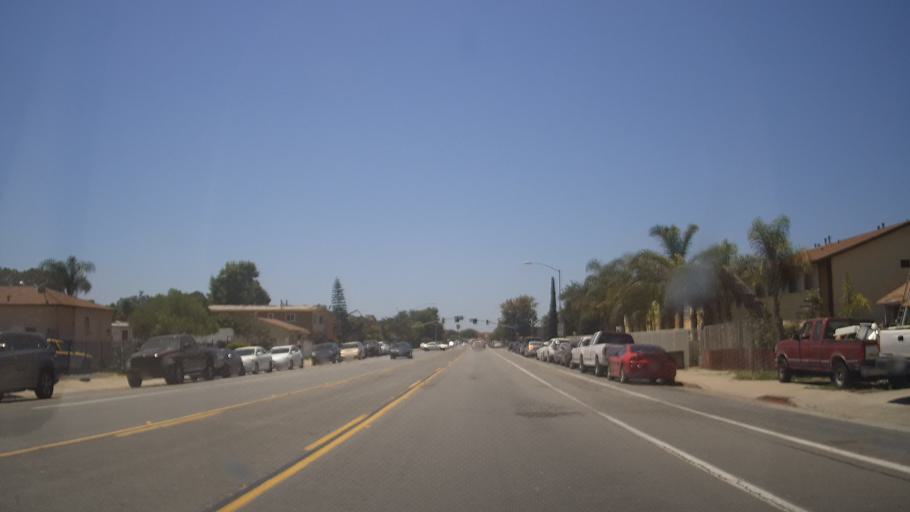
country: US
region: California
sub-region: San Diego County
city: National City
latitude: 32.7076
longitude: -117.0769
